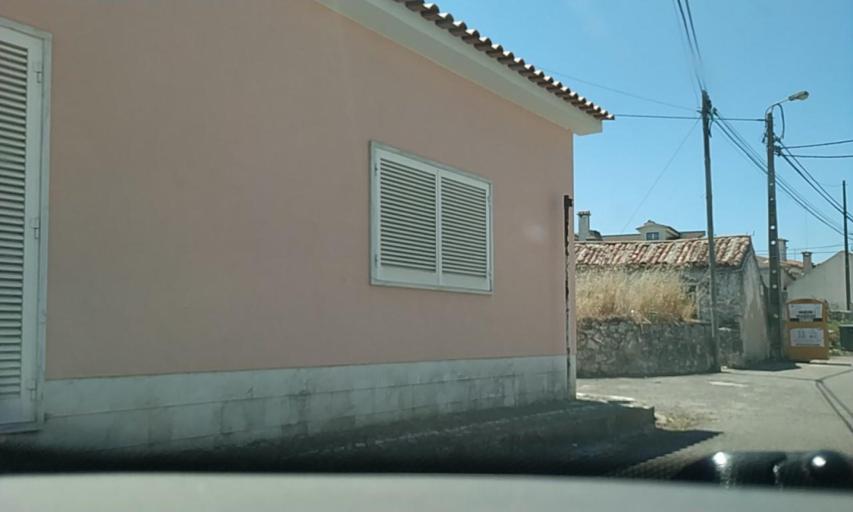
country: PT
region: Lisbon
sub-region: Sintra
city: Pero Pinheiro
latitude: 38.8656
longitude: -9.3135
